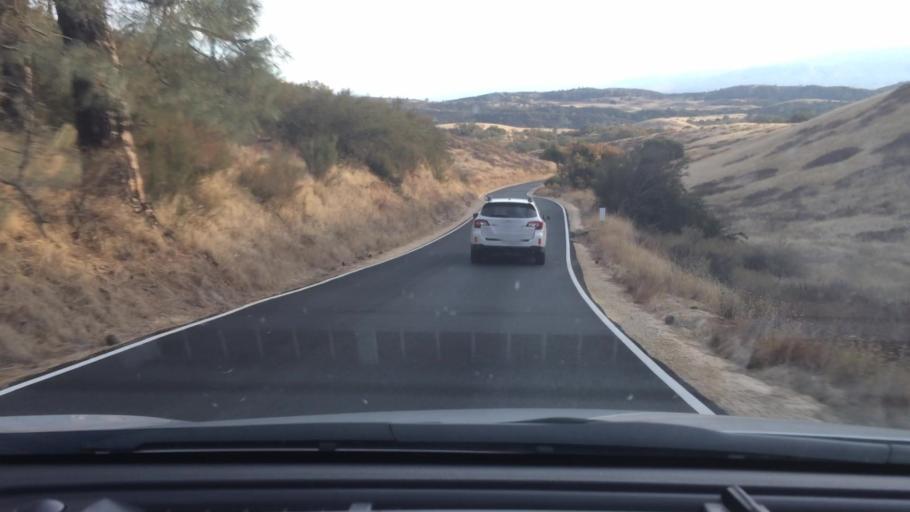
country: US
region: California
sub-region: Monterey County
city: Soledad
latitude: 36.4707
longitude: -121.2224
